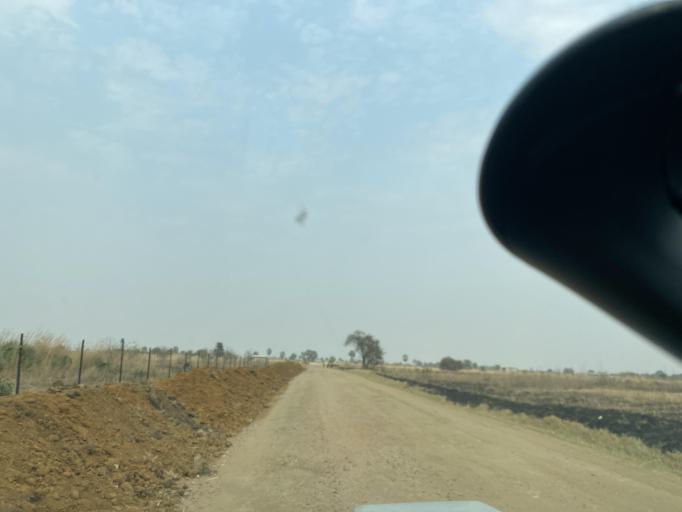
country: ZM
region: Lusaka
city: Kafue
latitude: -15.6453
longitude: 28.0813
